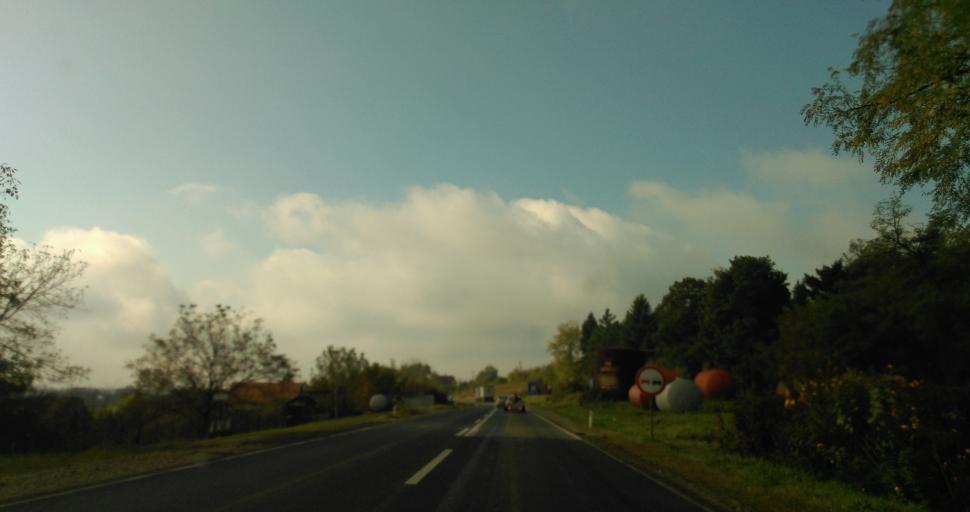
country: RS
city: Stepojevac
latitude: 44.5597
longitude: 20.3000
